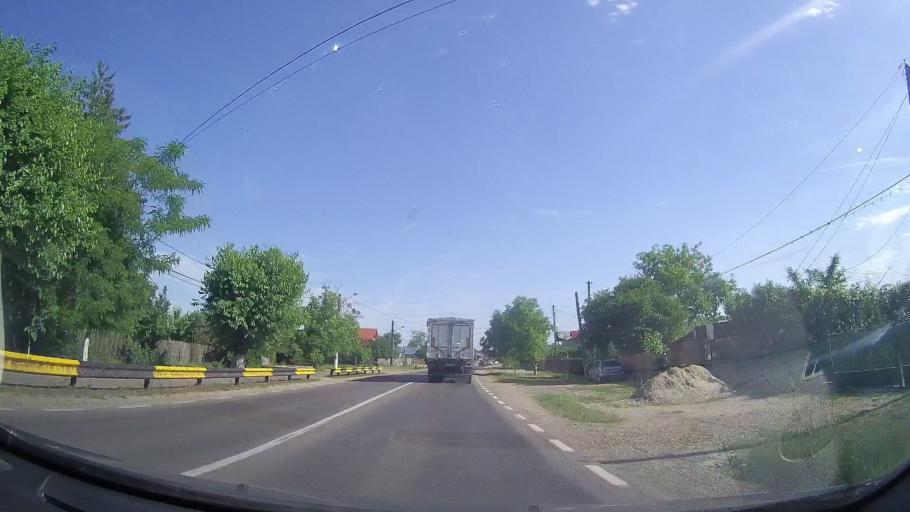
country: RO
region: Prahova
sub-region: Comuna Lipanesti
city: Sipotu
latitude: 45.0324
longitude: 26.0178
